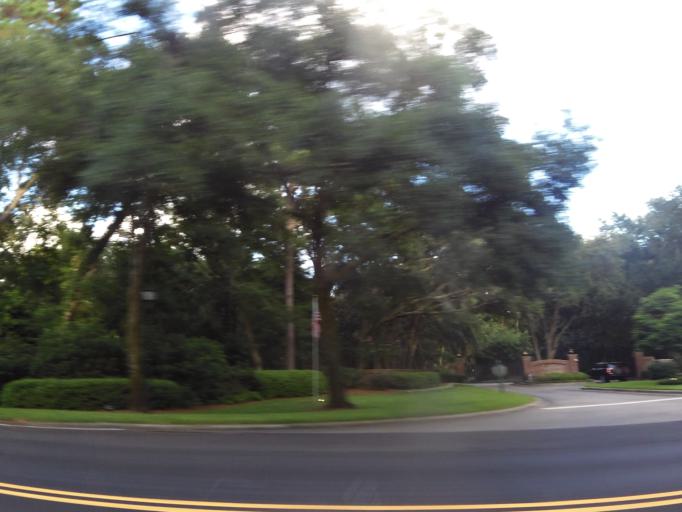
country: US
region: Georgia
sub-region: Glynn County
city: Saint Simon Mills
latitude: 31.1744
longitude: -81.4014
